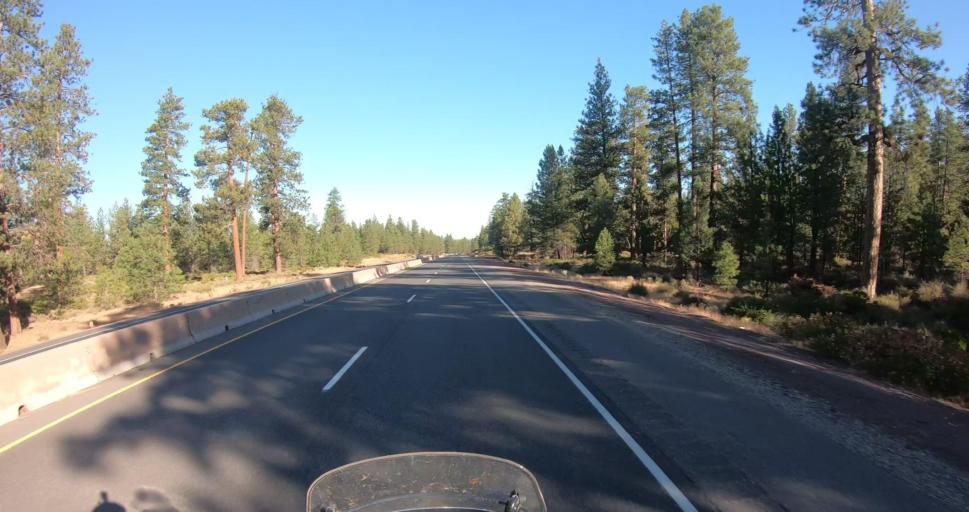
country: US
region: Oregon
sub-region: Deschutes County
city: Deschutes River Woods
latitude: 43.9219
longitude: -121.3507
